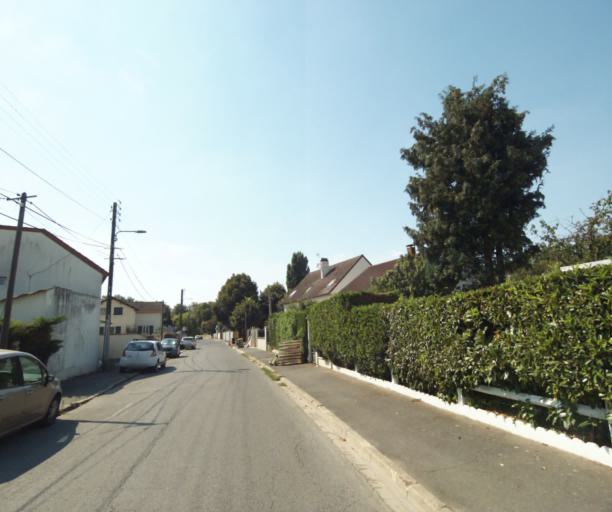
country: FR
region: Ile-de-France
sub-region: Departement de Seine-et-Marne
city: Pomponne
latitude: 48.8788
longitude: 2.6896
